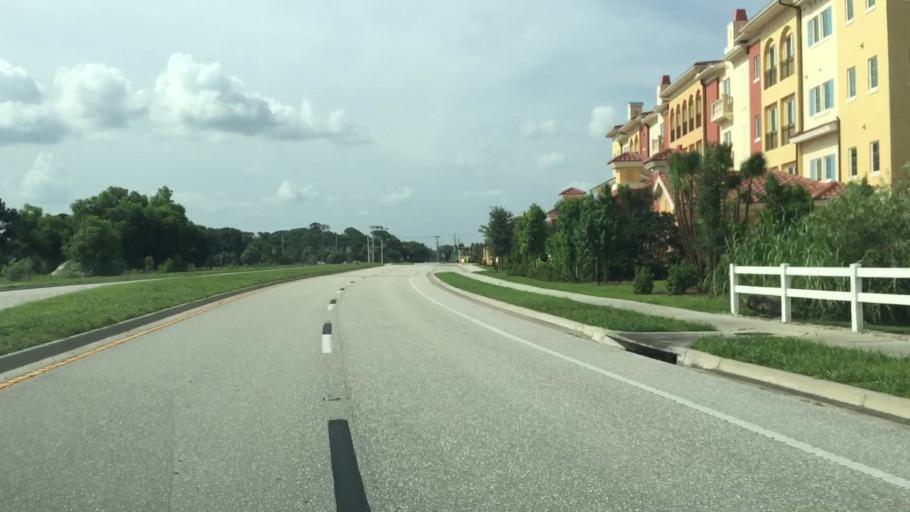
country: US
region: Florida
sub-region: Lee County
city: Estero
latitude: 26.4276
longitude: -81.8047
